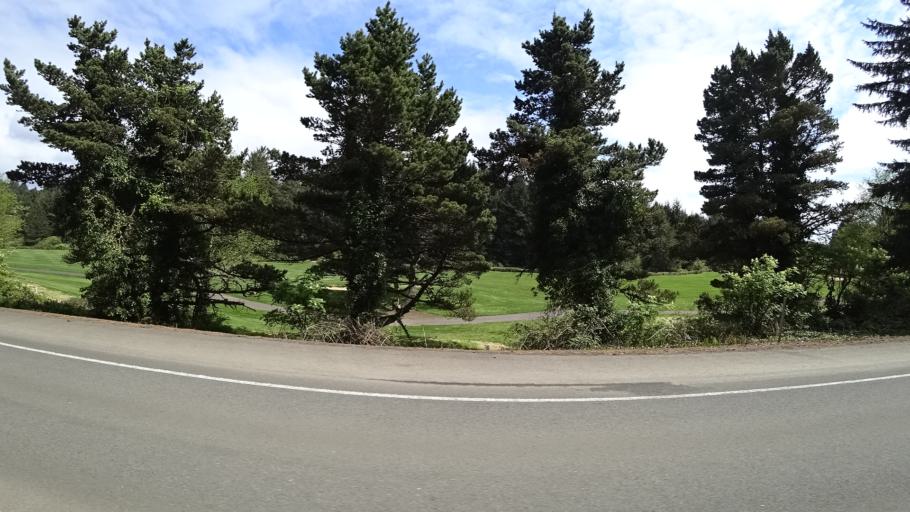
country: US
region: Oregon
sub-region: Lincoln County
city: Lincoln Beach
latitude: 44.8863
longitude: -124.0279
